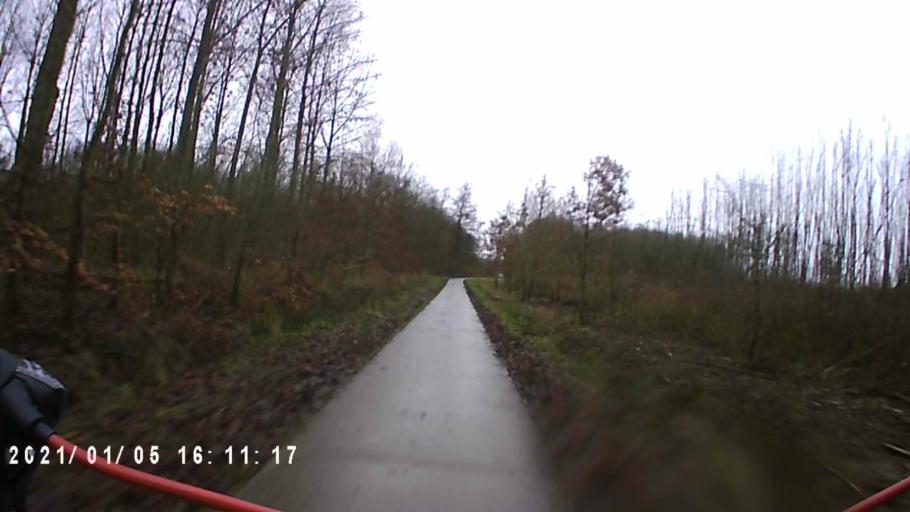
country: NL
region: Groningen
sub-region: Gemeente  Oldambt
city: Winschoten
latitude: 53.1949
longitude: 7.0761
